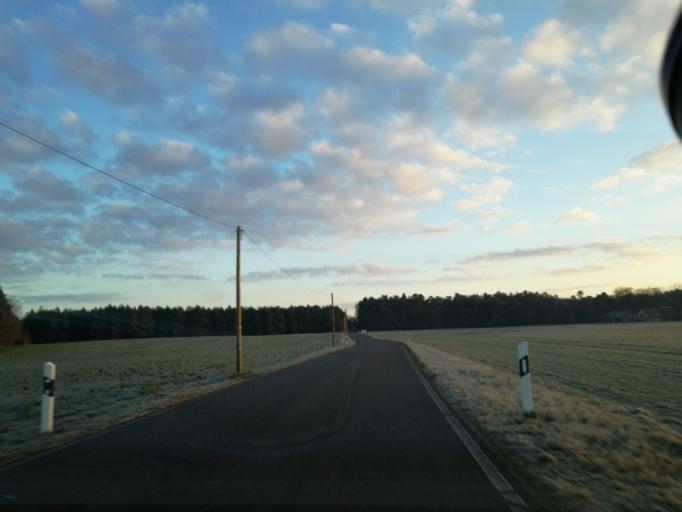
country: DE
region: Brandenburg
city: Crinitz
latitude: 51.7388
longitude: 13.8296
